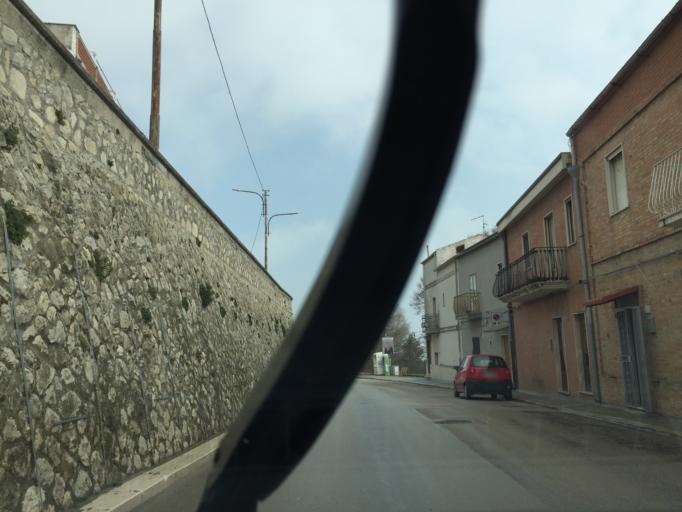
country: IT
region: Apulia
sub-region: Provincia di Foggia
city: Troia
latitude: 41.3614
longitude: 15.3115
